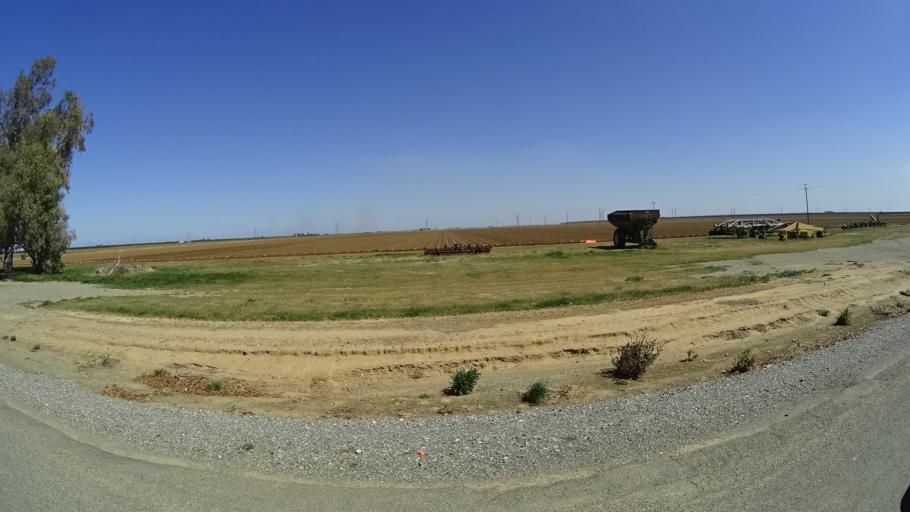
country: US
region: California
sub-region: Glenn County
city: Willows
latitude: 39.4860
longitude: -122.2773
